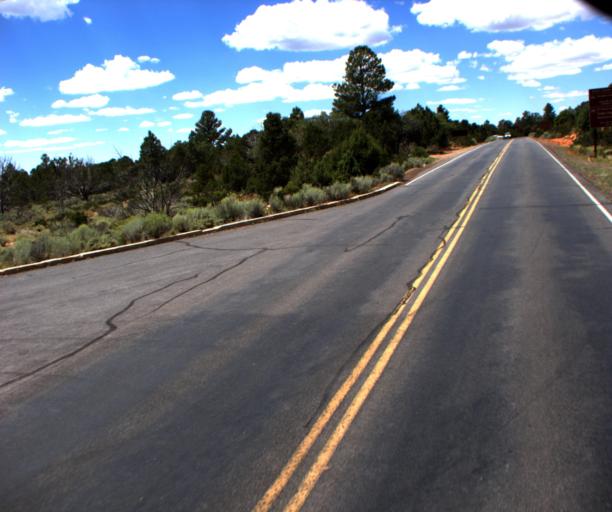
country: US
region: Arizona
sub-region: Coconino County
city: Grand Canyon
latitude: 36.0513
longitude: -112.1034
